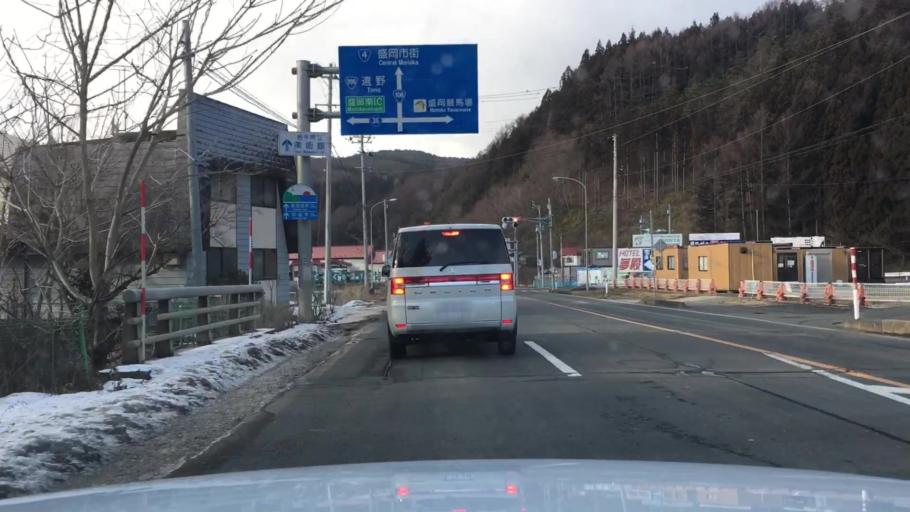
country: JP
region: Iwate
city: Morioka-shi
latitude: 39.6739
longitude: 141.2109
